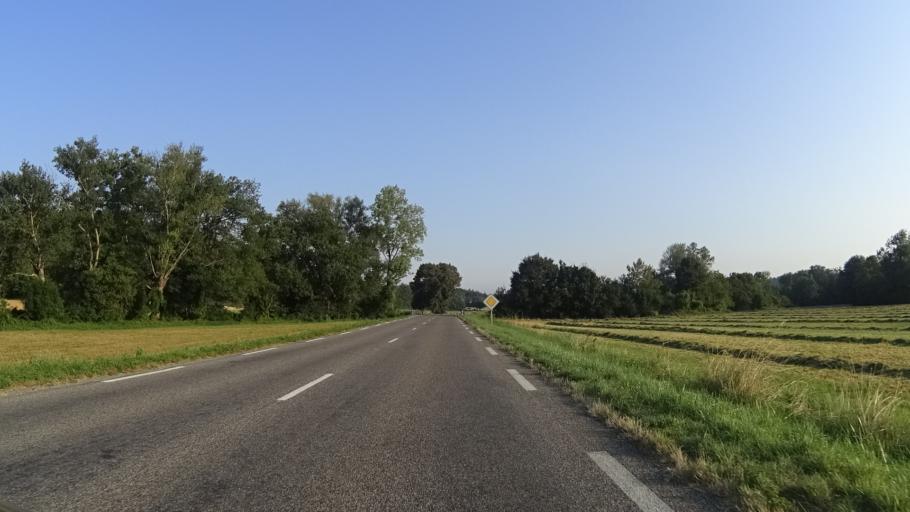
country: FR
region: Midi-Pyrenees
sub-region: Departement de l'Ariege
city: Mirepoix
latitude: 43.0593
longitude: 1.8830
